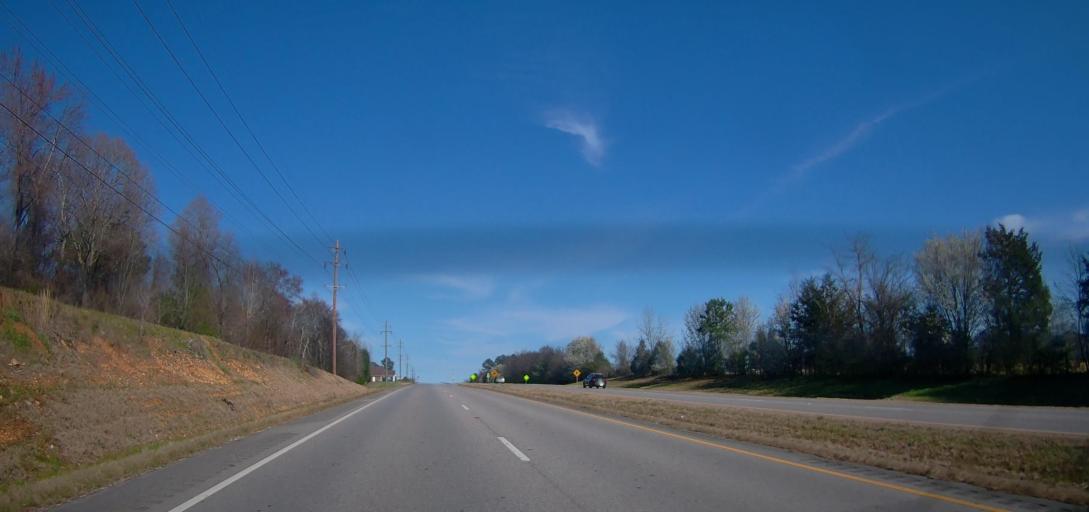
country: US
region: Alabama
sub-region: Lauderdale County
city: Killen
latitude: 34.8598
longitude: -87.5040
